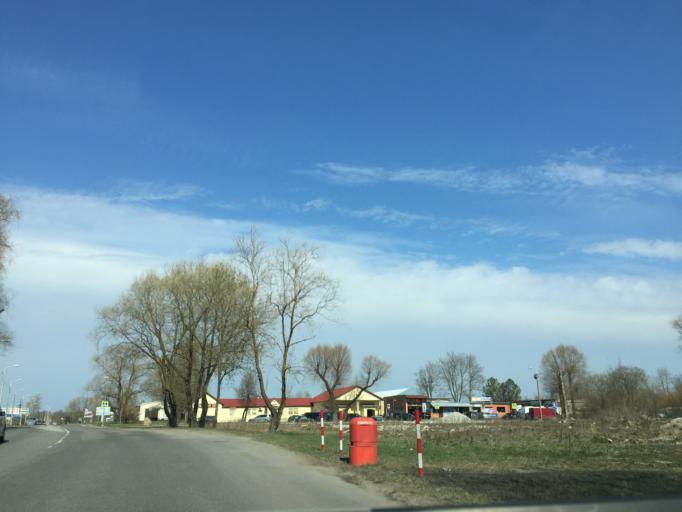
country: EE
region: Ida-Virumaa
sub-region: Narva linn
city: Narva
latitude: 59.3869
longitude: 28.1889
